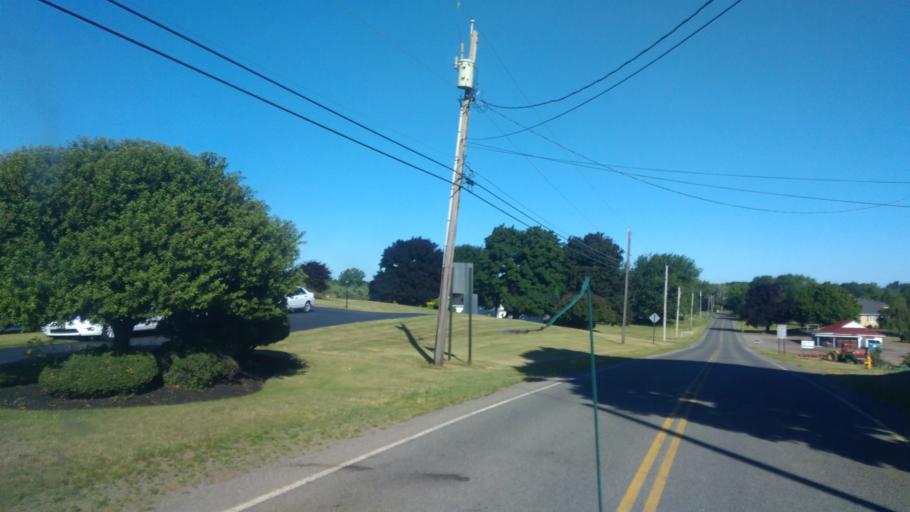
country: US
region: New York
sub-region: Wayne County
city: Williamson
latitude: 43.2815
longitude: -77.1310
